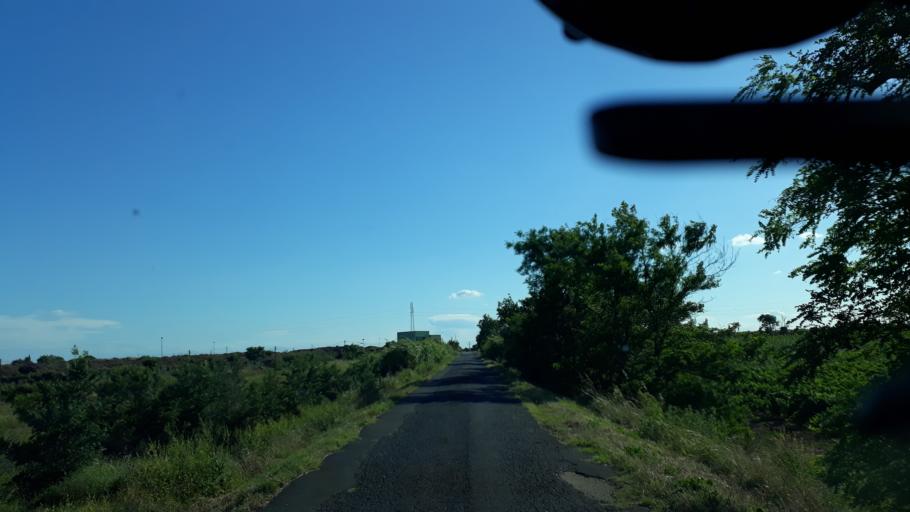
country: FR
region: Languedoc-Roussillon
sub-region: Departement de l'Herault
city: Agde
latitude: 43.3253
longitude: 3.4952
